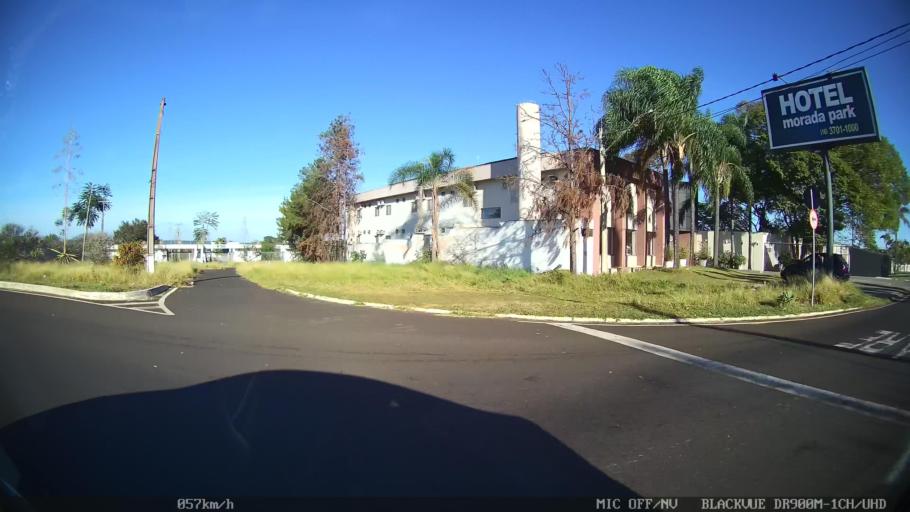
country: BR
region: Sao Paulo
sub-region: Franca
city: Franca
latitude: -20.5749
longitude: -47.3893
